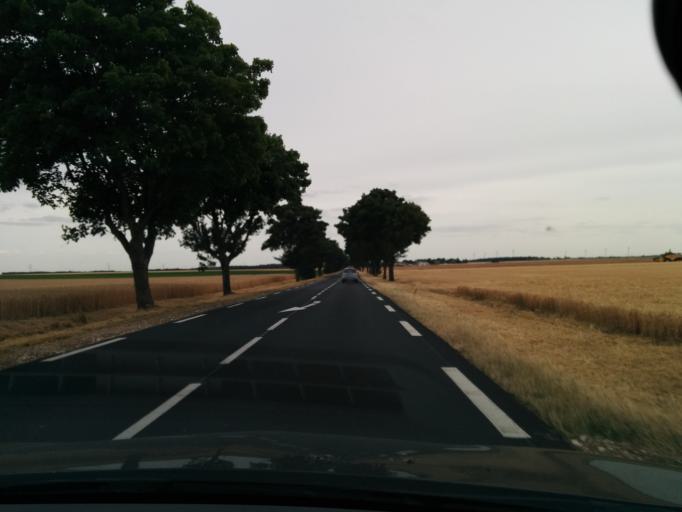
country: FR
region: Ile-de-France
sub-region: Departement de l'Essonne
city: Pussay
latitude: 48.3872
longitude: 1.9749
